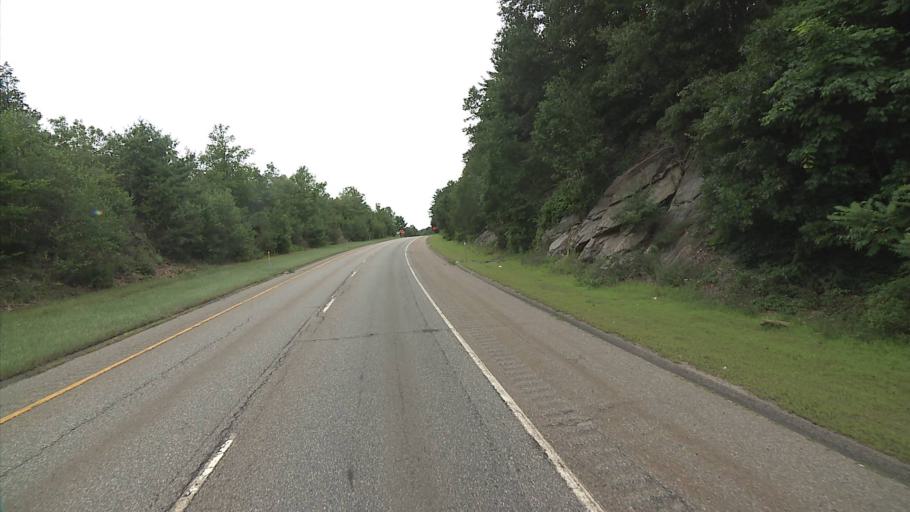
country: US
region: Connecticut
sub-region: Litchfield County
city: Thomaston
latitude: 41.7169
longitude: -73.0932
